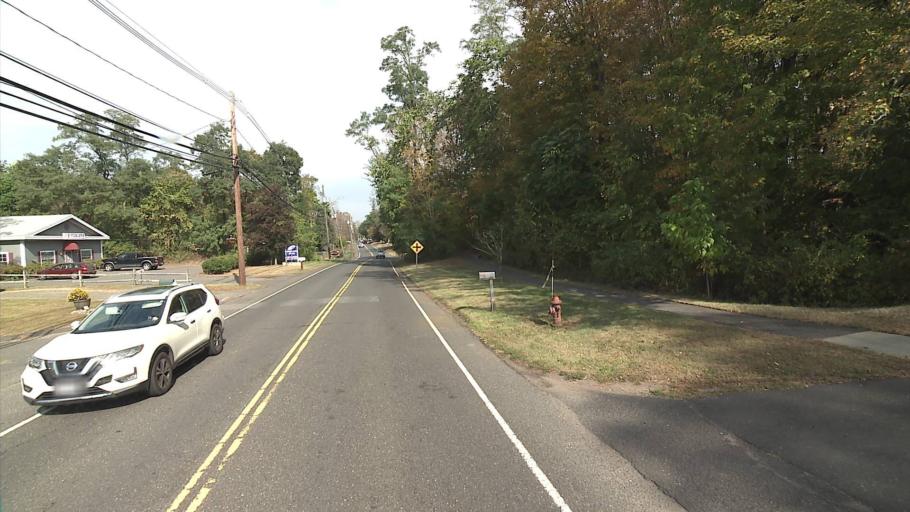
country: US
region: Connecticut
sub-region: Litchfield County
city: Woodbury Center
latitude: 41.5307
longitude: -73.2047
